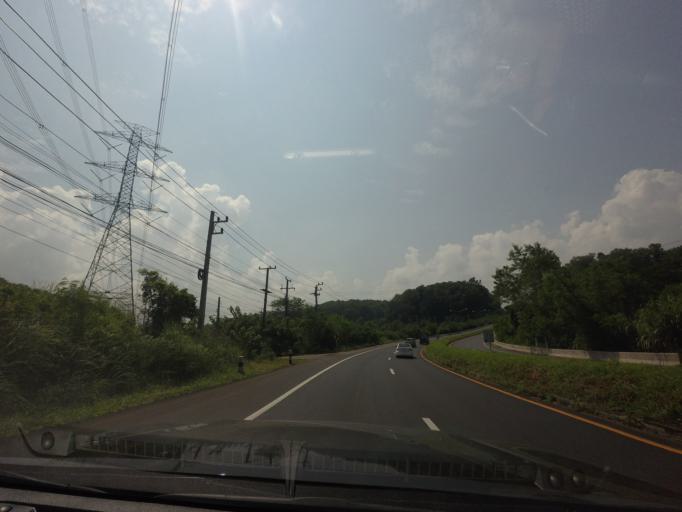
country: TH
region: Phrae
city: Den Chai
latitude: 17.8873
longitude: 100.0492
